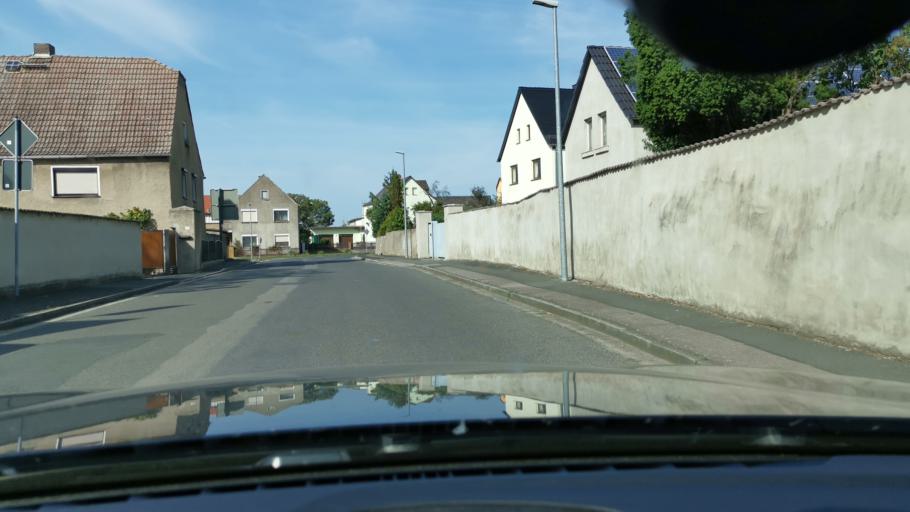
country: DE
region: Saxony
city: Mockrehna
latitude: 51.4705
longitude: 12.8086
